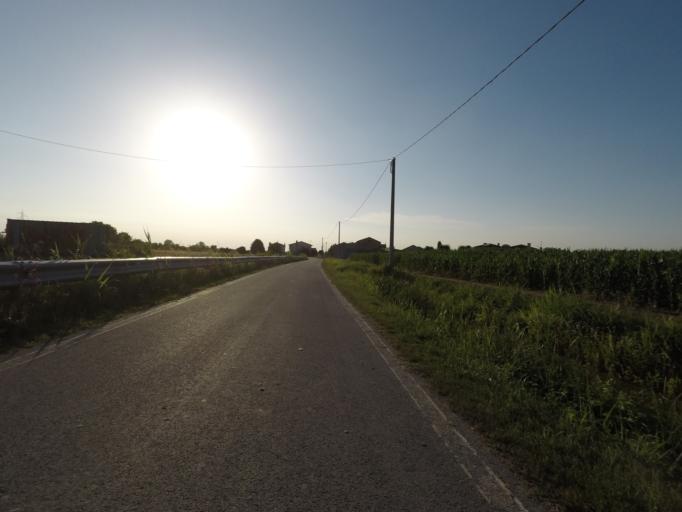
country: IT
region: Veneto
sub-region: Provincia di Rovigo
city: Villamarzana
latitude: 45.0327
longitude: 11.6745
